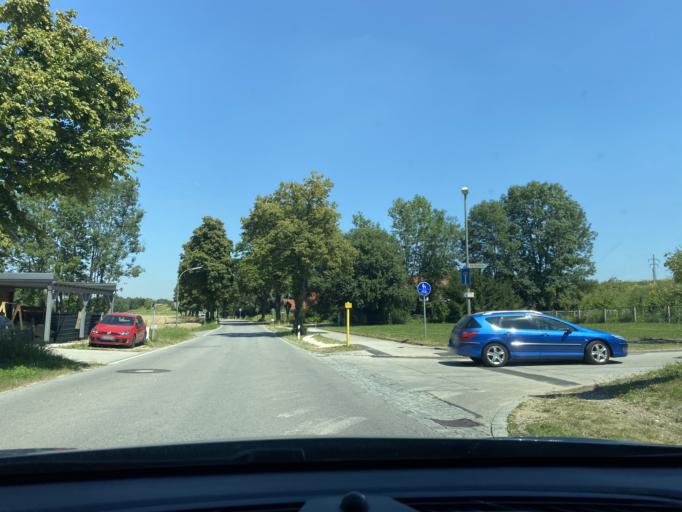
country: DE
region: Bavaria
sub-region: Upper Bavaria
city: Moosinning
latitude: 48.2560
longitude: 11.8468
